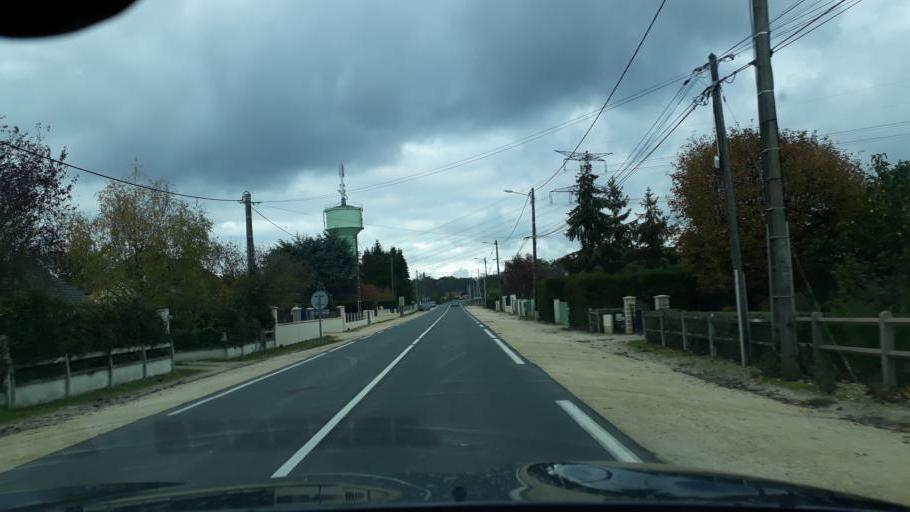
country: FR
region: Centre
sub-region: Departement du Loiret
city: Bray-en-Val
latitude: 47.8187
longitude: 2.4067
